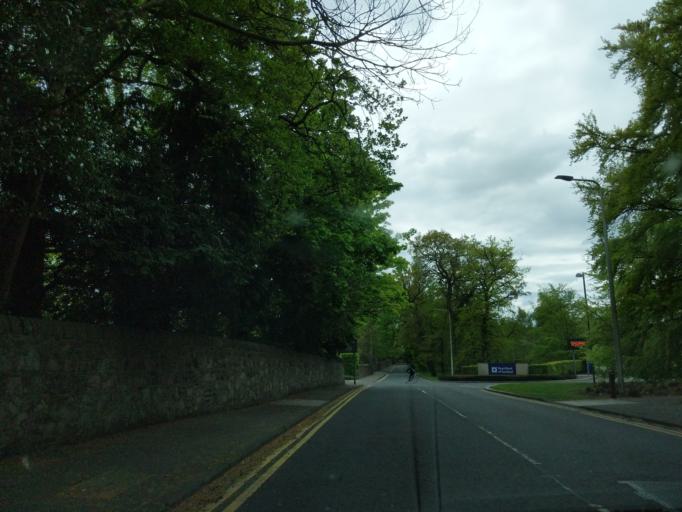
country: GB
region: Scotland
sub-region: Edinburgh
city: Currie
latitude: 55.9371
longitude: -3.3317
